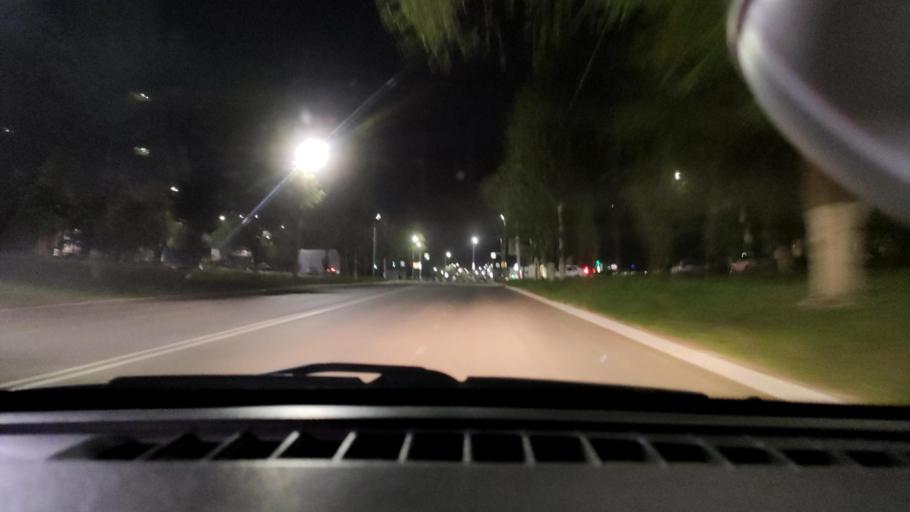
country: RU
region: Samara
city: Novokuybyshevsk
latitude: 53.0974
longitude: 49.9741
